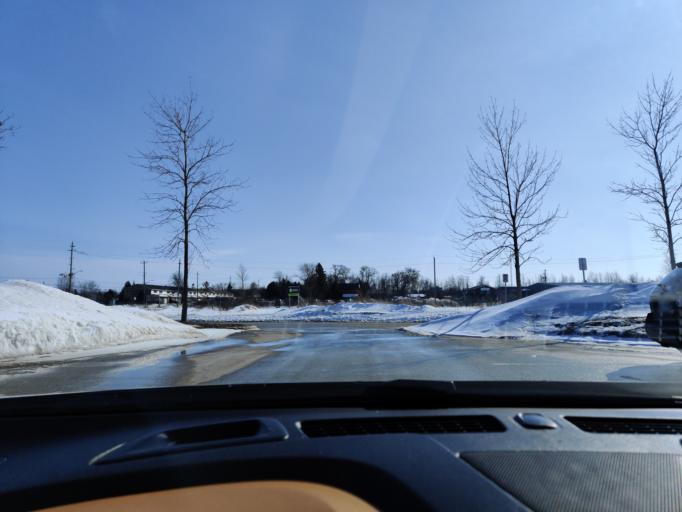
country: CA
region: Ontario
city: Collingwood
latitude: 44.4985
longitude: -80.2348
